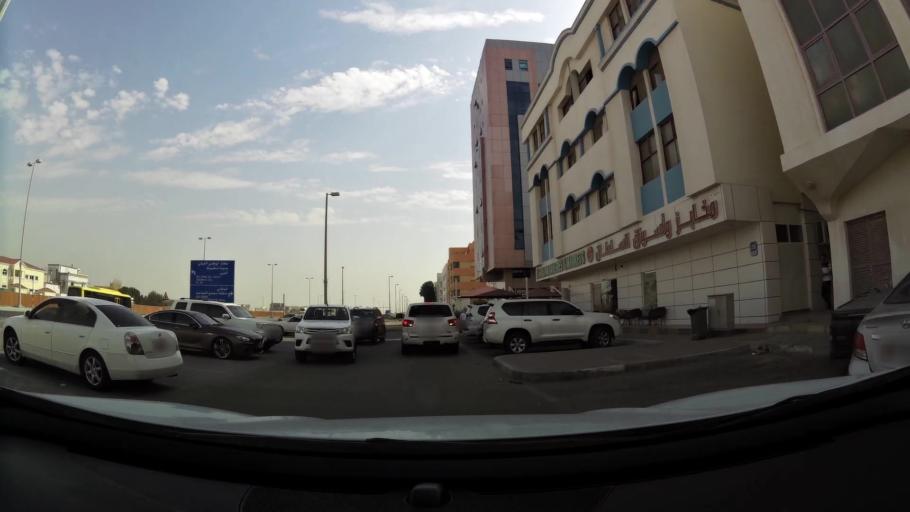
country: AE
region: Abu Dhabi
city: Abu Dhabi
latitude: 24.3277
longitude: 54.5386
